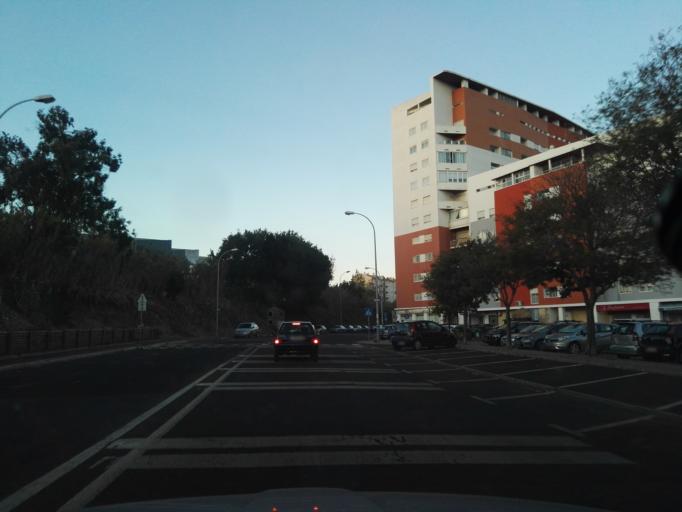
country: PT
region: Lisbon
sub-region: Amadora
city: Amadora
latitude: 38.7348
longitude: -9.2154
